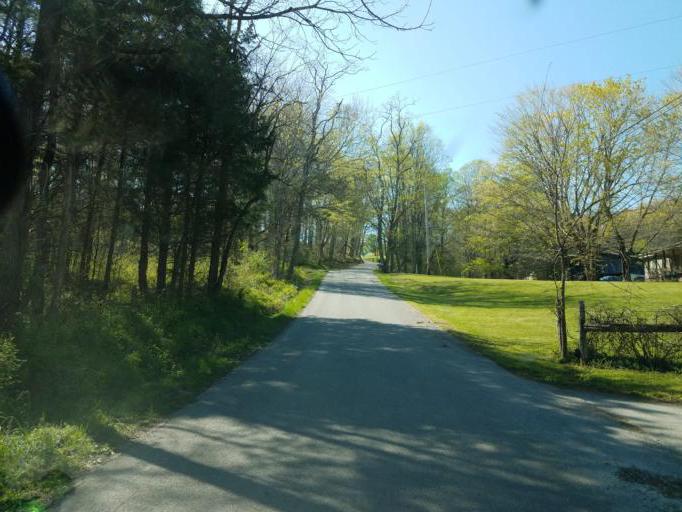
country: US
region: Kentucky
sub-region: Edmonson County
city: Brownsville
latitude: 37.1208
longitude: -86.1371
